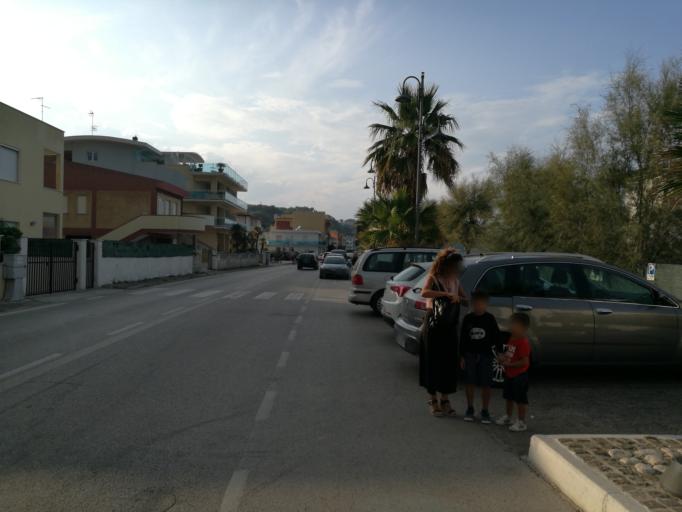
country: IT
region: Abruzzo
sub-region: Provincia di Chieti
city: Fossacesia
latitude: 42.2490
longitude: 14.5127
